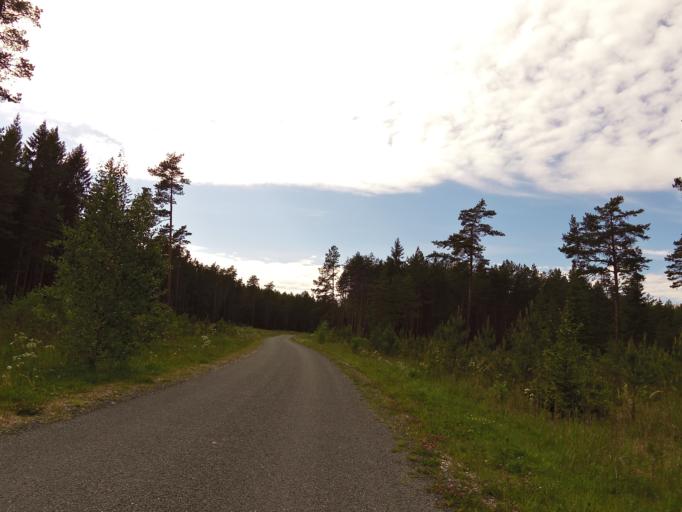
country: EE
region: Harju
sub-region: Paldiski linn
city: Paldiski
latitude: 59.2496
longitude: 23.7701
